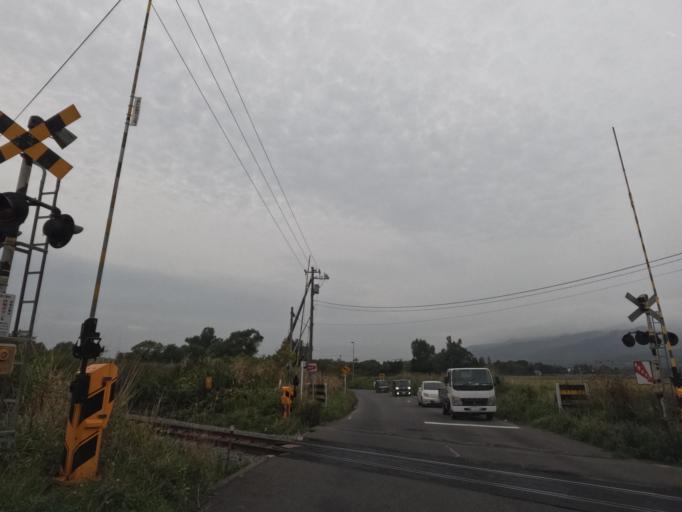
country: JP
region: Hokkaido
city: Date
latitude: 42.4378
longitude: 140.8910
